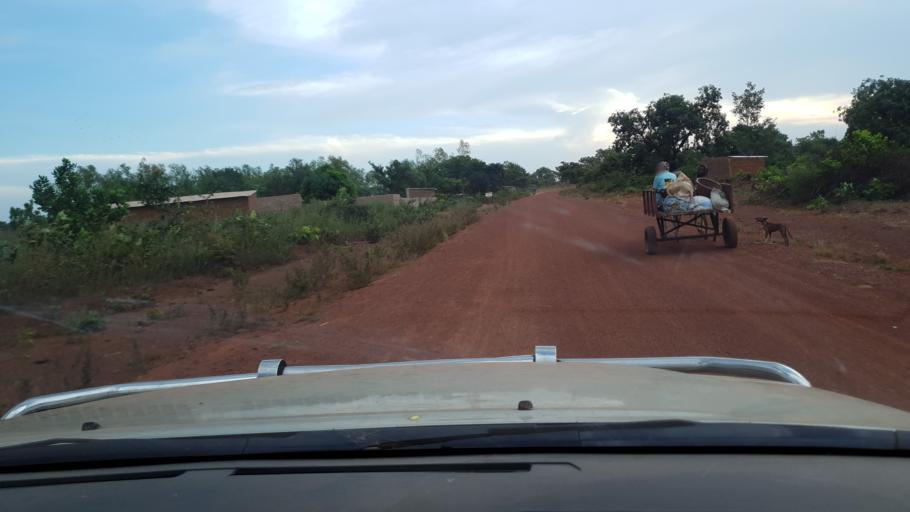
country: ML
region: Sikasso
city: Kolondieba
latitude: 11.4416
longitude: -6.3407
